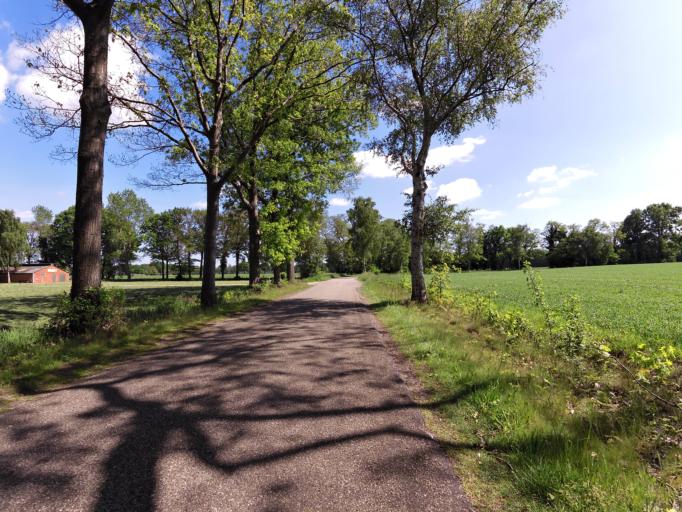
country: NL
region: Gelderland
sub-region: Gemeente Bronckhorst
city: Hengelo
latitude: 52.0778
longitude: 6.3734
